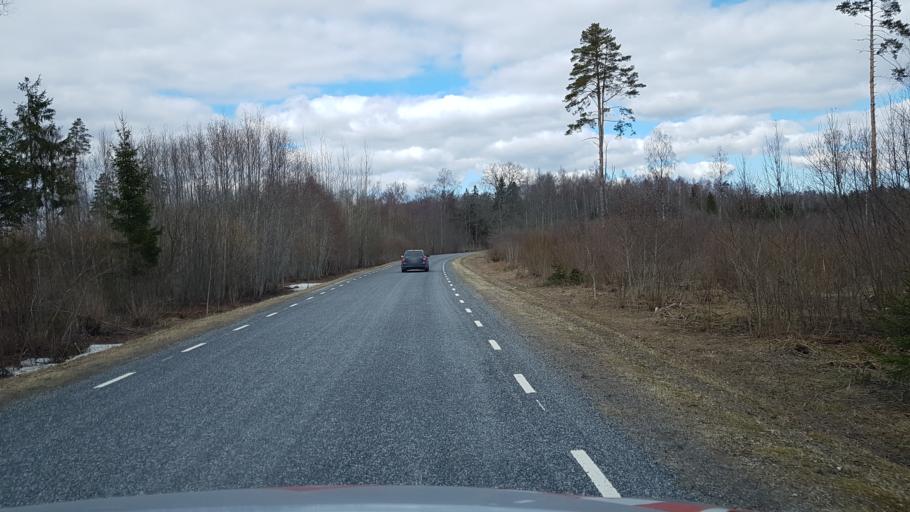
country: EE
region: Laeaene-Virumaa
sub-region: Tamsalu vald
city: Tamsalu
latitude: 59.1894
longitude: 26.1302
